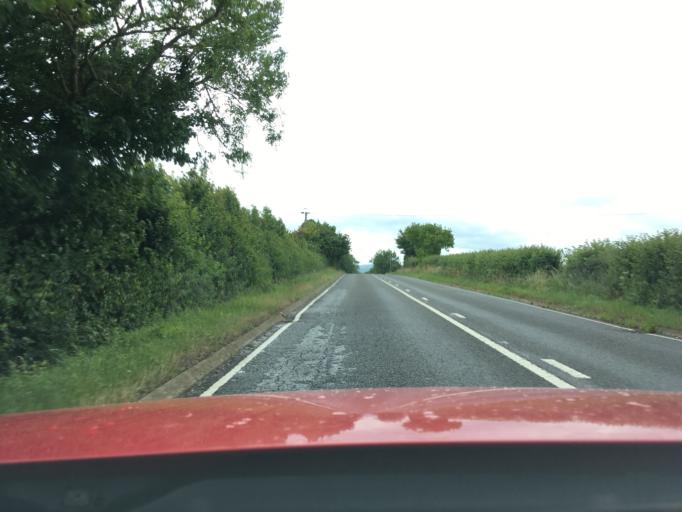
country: GB
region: England
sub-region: Warwickshire
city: Shipston on Stour
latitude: 52.1207
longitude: -1.6084
